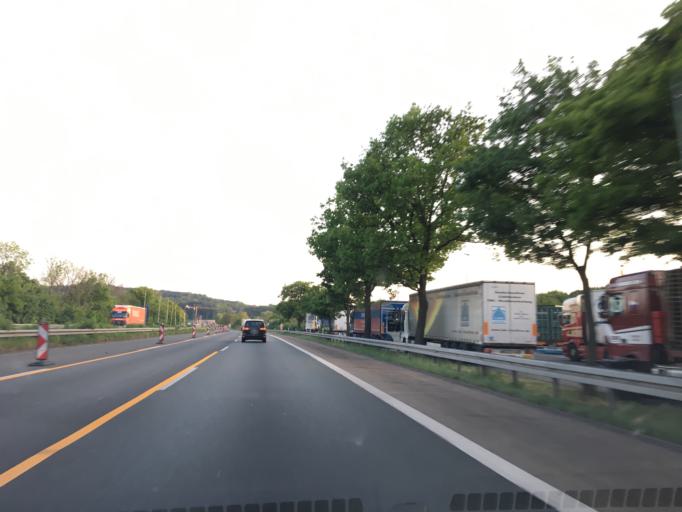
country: DE
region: North Rhine-Westphalia
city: Lengerich
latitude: 52.2318
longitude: 7.8788
